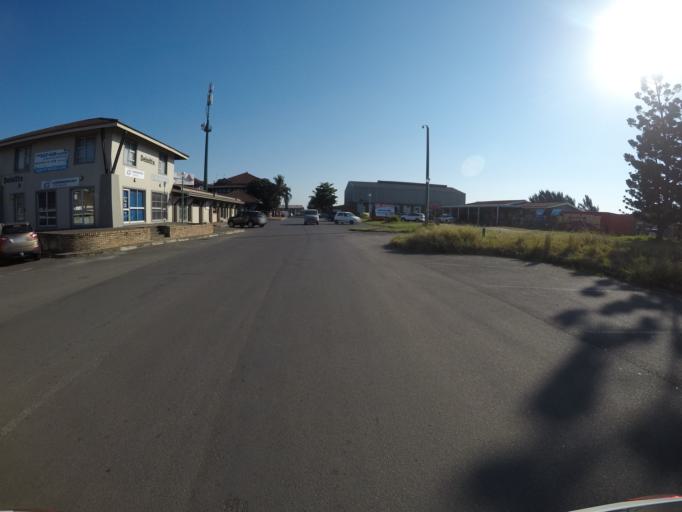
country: ZA
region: KwaZulu-Natal
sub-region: uThungulu District Municipality
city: Richards Bay
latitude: -28.7929
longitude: 32.0797
